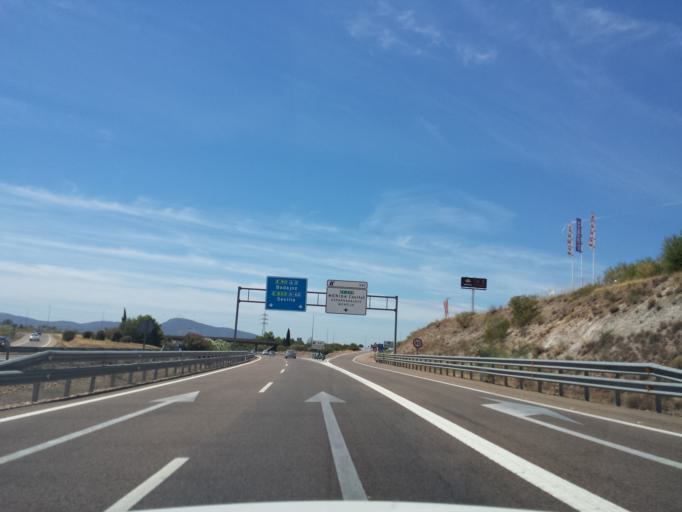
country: ES
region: Extremadura
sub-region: Provincia de Badajoz
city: Merida
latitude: 38.9395
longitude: -6.3619
